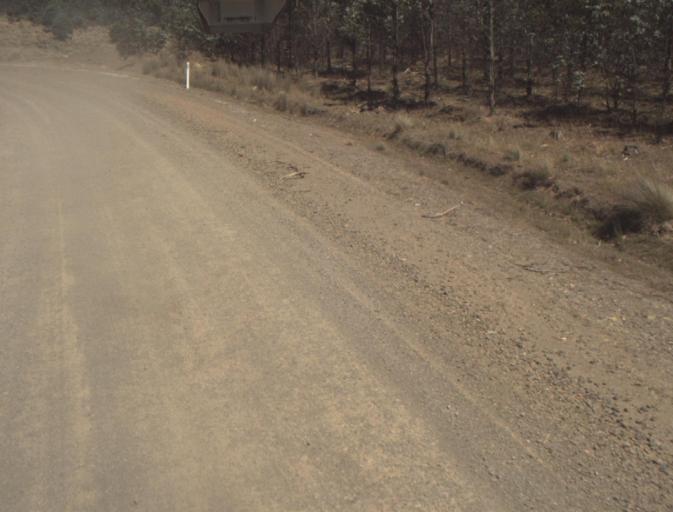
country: AU
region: Tasmania
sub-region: Dorset
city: Scottsdale
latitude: -41.3702
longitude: 147.4706
